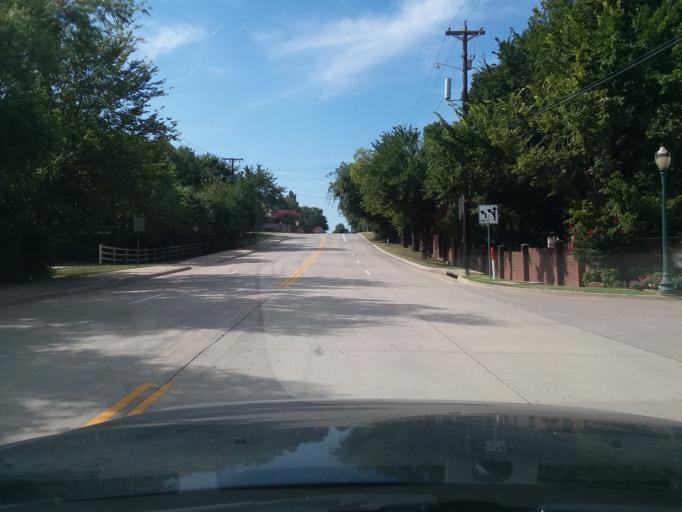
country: US
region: Texas
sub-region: Denton County
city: Flower Mound
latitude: 33.0150
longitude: -97.0885
